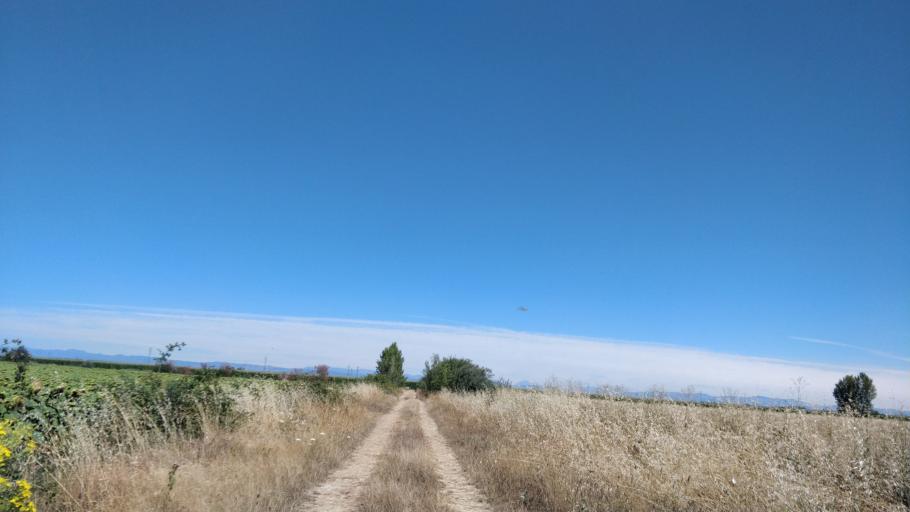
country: ES
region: Castille and Leon
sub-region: Provincia de Leon
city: Bustillo del Paramo
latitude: 42.4501
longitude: -5.8168
